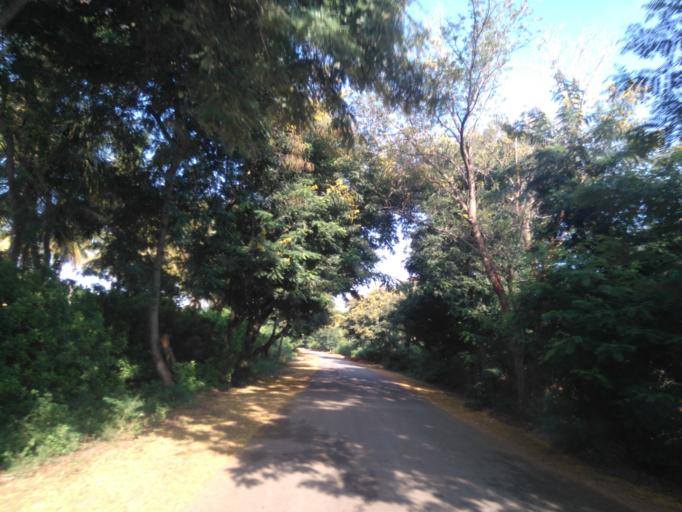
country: IN
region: Karnataka
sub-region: Mandya
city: Malavalli
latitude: 12.2636
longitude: 77.0350
